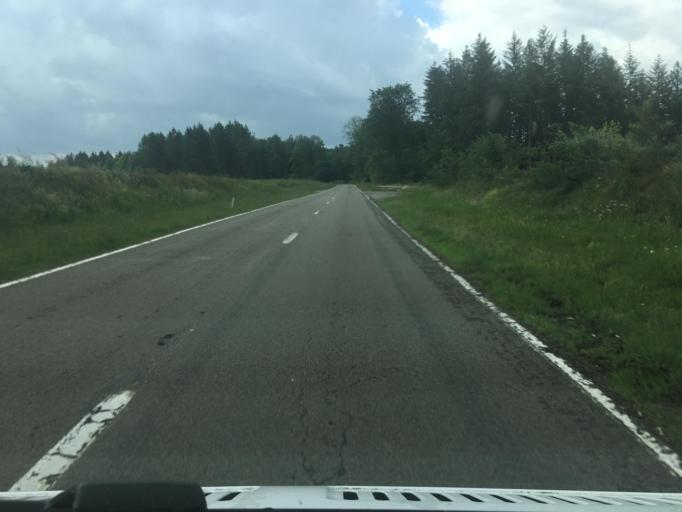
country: BE
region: Wallonia
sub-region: Province du Luxembourg
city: Florenville
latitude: 49.6512
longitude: 5.3382
